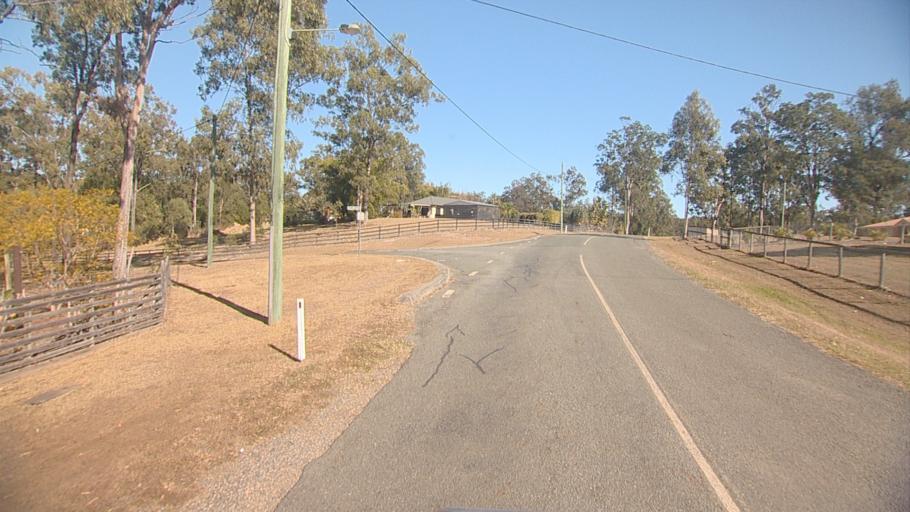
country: AU
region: Queensland
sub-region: Logan
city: Cedar Vale
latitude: -27.8823
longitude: 153.0037
